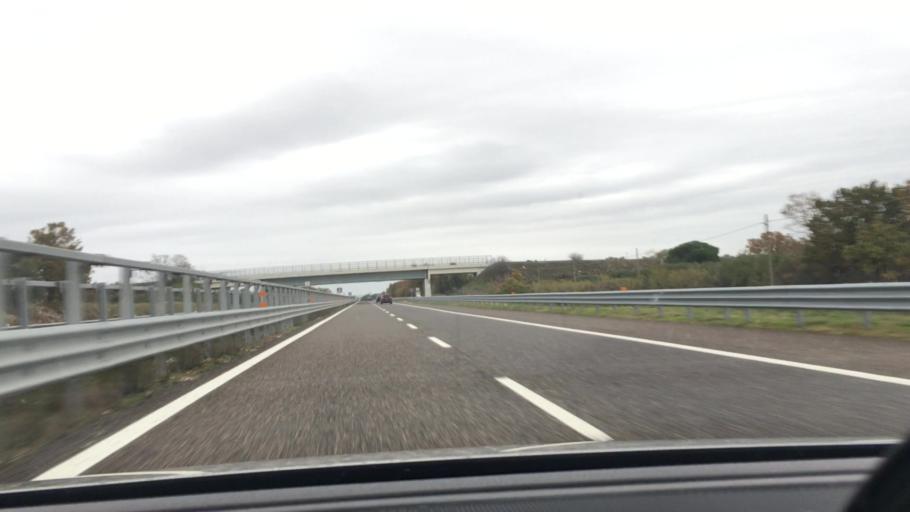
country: IT
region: Apulia
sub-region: Provincia di Bari
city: Gioia del Colle
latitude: 40.7482
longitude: 16.9156
